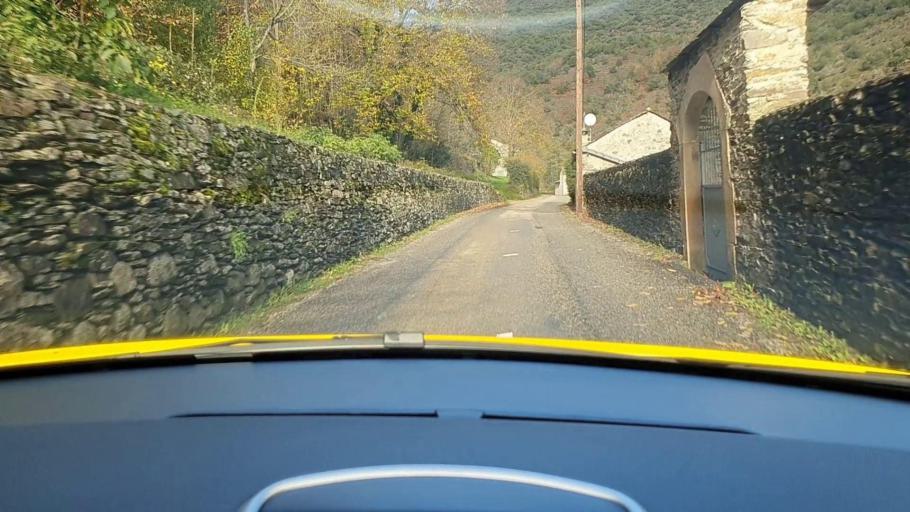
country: FR
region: Languedoc-Roussillon
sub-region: Departement du Gard
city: Valleraugue
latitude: 44.1601
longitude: 3.6746
